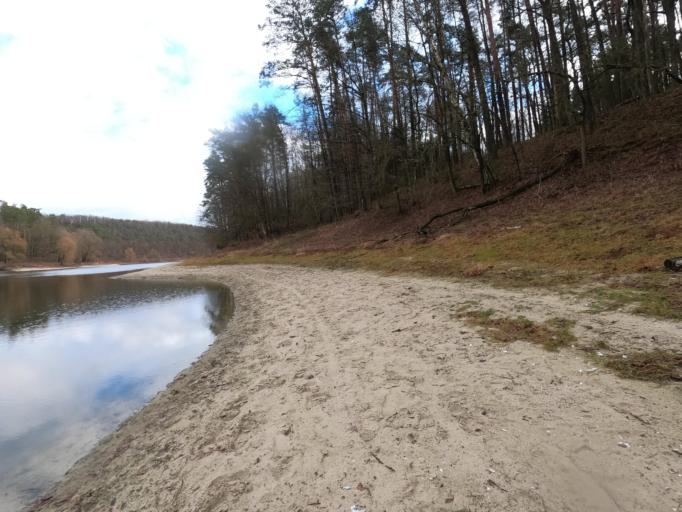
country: PL
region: Greater Poland Voivodeship
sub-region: Powiat pilski
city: Kaczory
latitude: 53.1104
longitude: 16.8985
